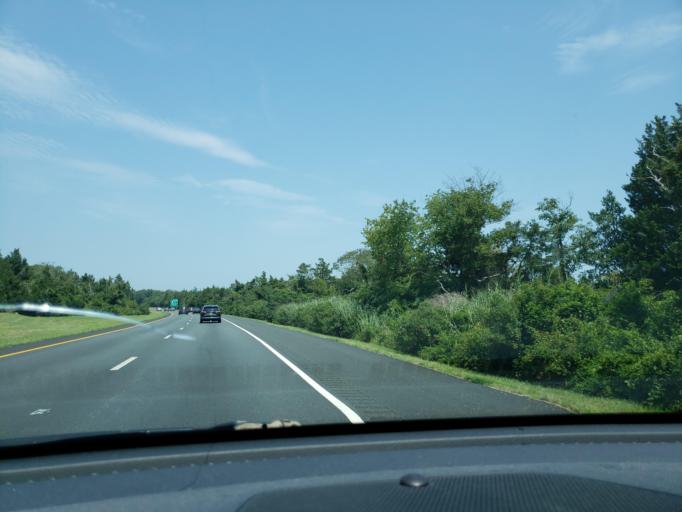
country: US
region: New Jersey
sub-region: Atlantic County
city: Somers Point
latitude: 39.2763
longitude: -74.6282
